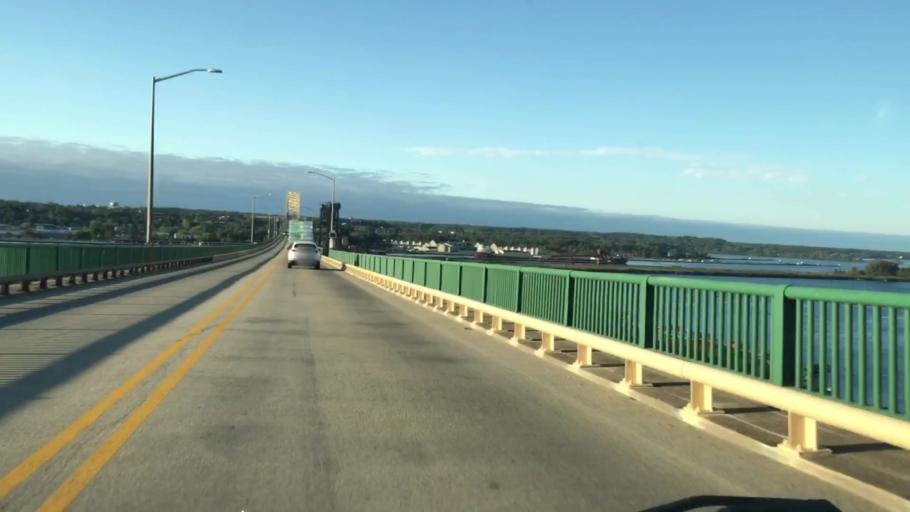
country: US
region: Michigan
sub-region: Chippewa County
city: Sault Ste. Marie
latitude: 46.5112
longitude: -84.3597
